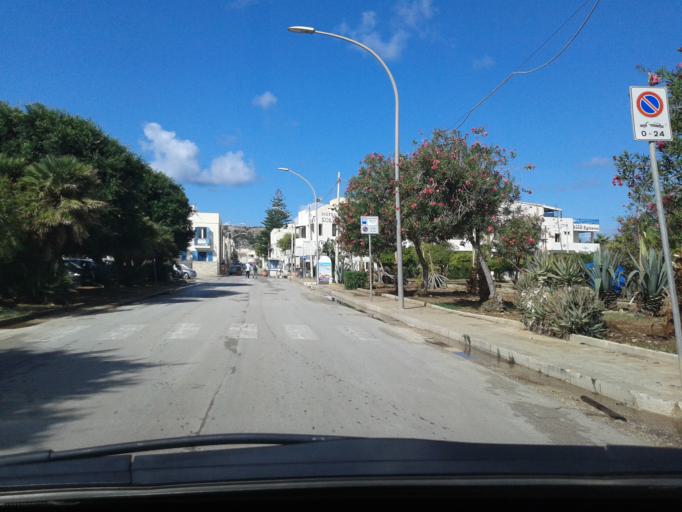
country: IT
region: Sicily
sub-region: Trapani
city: San Vito Lo Capo
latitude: 38.1747
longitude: 12.7399
